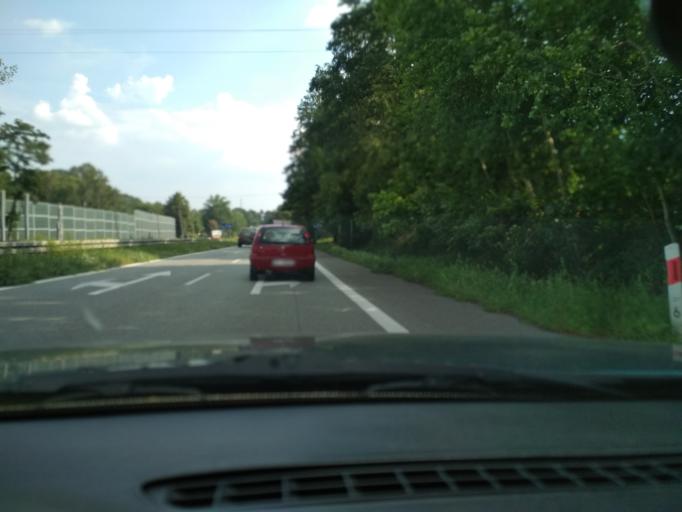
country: PL
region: Silesian Voivodeship
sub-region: Powiat pszczynski
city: Pawlowice
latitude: 49.9979
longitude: 18.7114
